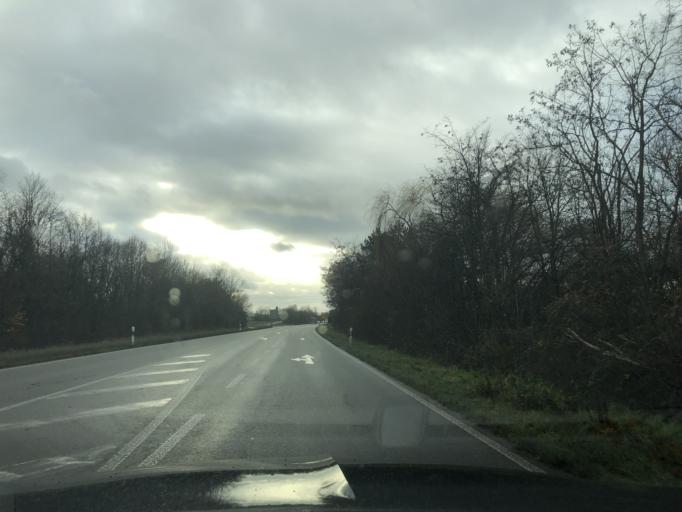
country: DE
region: Baden-Wuerttemberg
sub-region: Karlsruhe Region
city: Kronau
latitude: 49.2065
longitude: 8.6276
